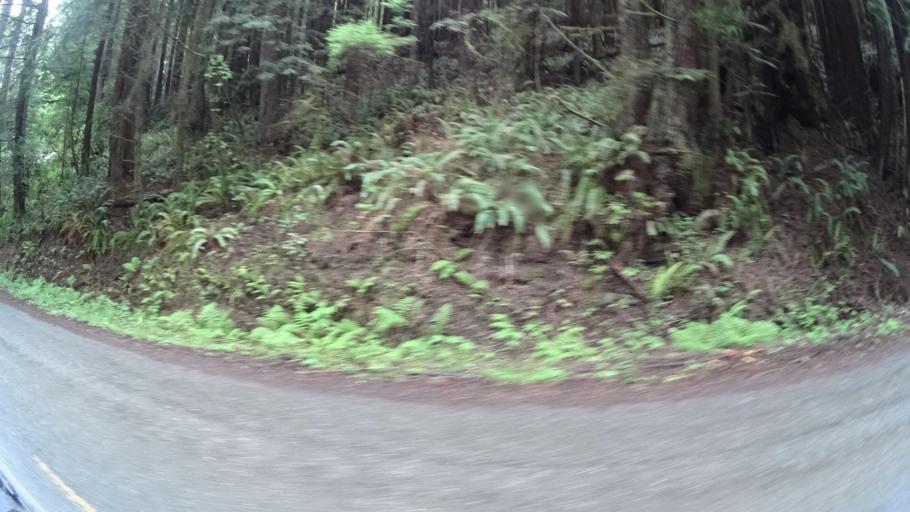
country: US
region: California
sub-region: Humboldt County
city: Bayside
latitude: 40.8214
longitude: -124.0319
